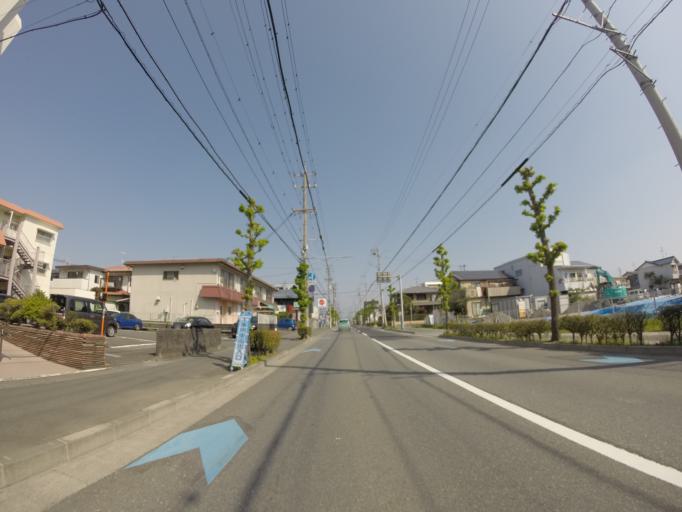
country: JP
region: Shizuoka
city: Shizuoka-shi
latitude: 34.9986
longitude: 138.4891
